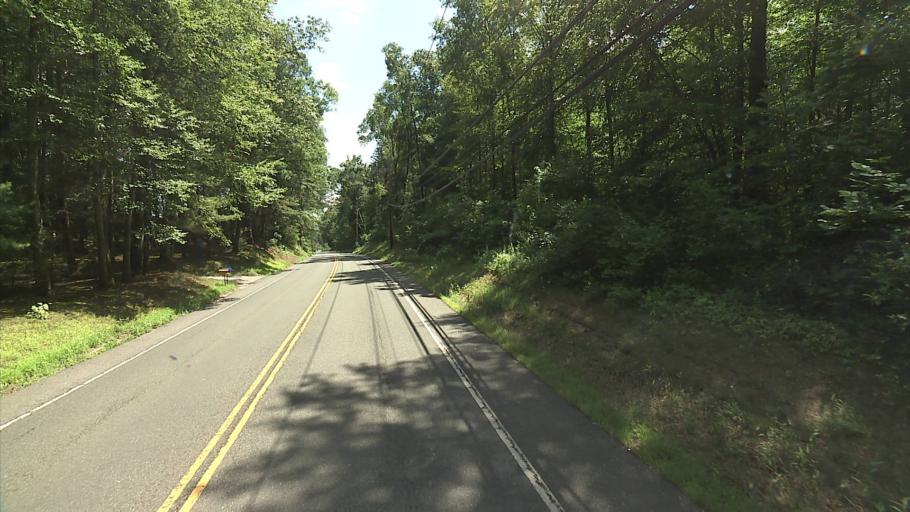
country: US
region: Massachusetts
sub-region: Hampden County
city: Southwick
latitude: 42.0004
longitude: -72.7252
